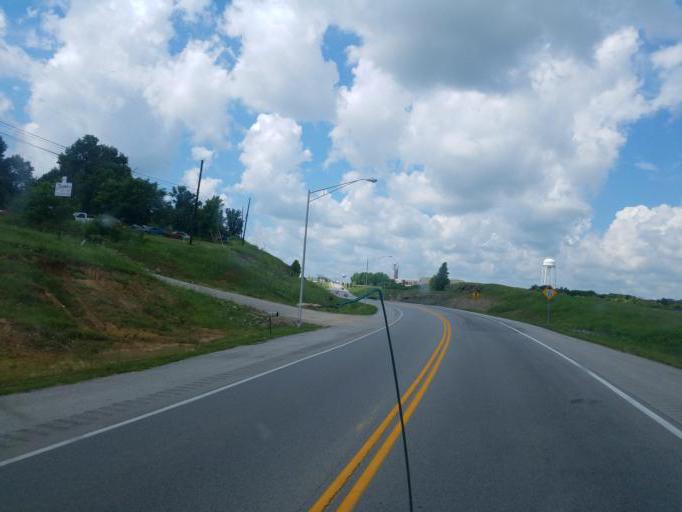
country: US
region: Kentucky
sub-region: Grayson County
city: Leitchfield
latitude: 37.4893
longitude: -86.2613
